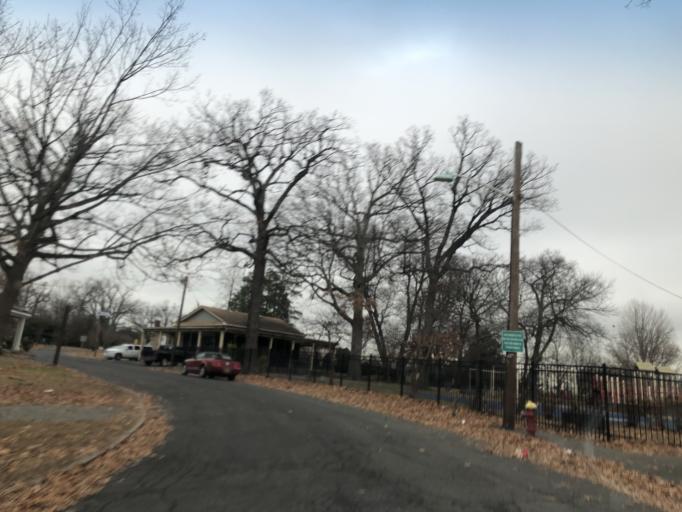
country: US
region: New Jersey
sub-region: Bergen County
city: Elmwood Park
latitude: 40.9153
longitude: -74.1385
